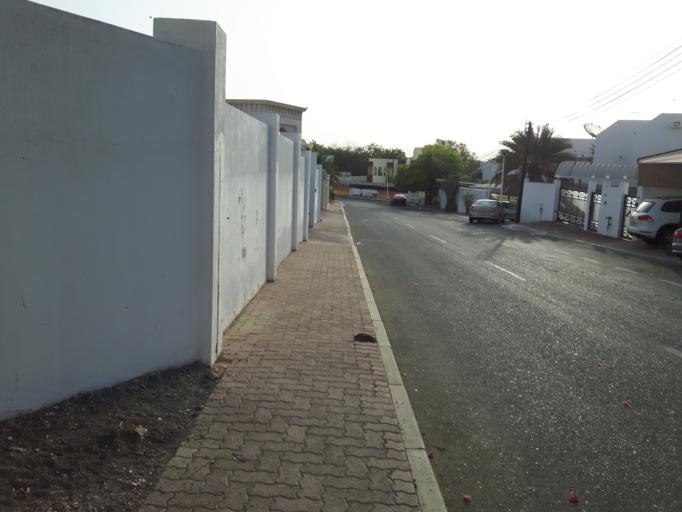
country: OM
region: Muhafazat Masqat
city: Bawshar
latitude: 23.6088
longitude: 58.4722
